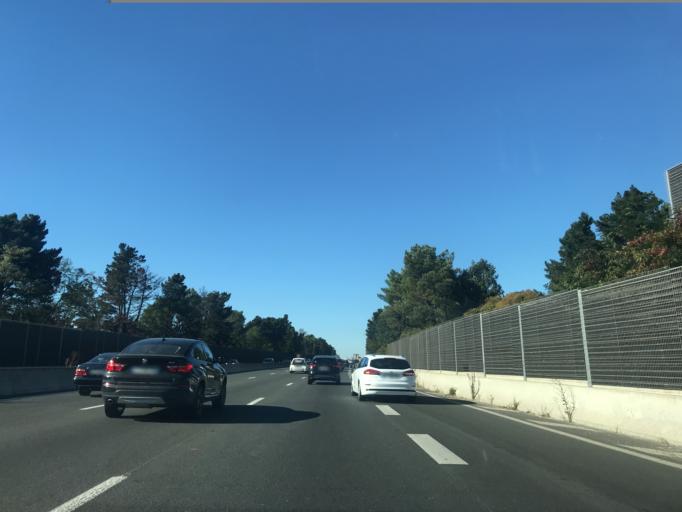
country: FR
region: Aquitaine
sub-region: Departement de la Gironde
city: Pessac
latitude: 44.7916
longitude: -0.6479
